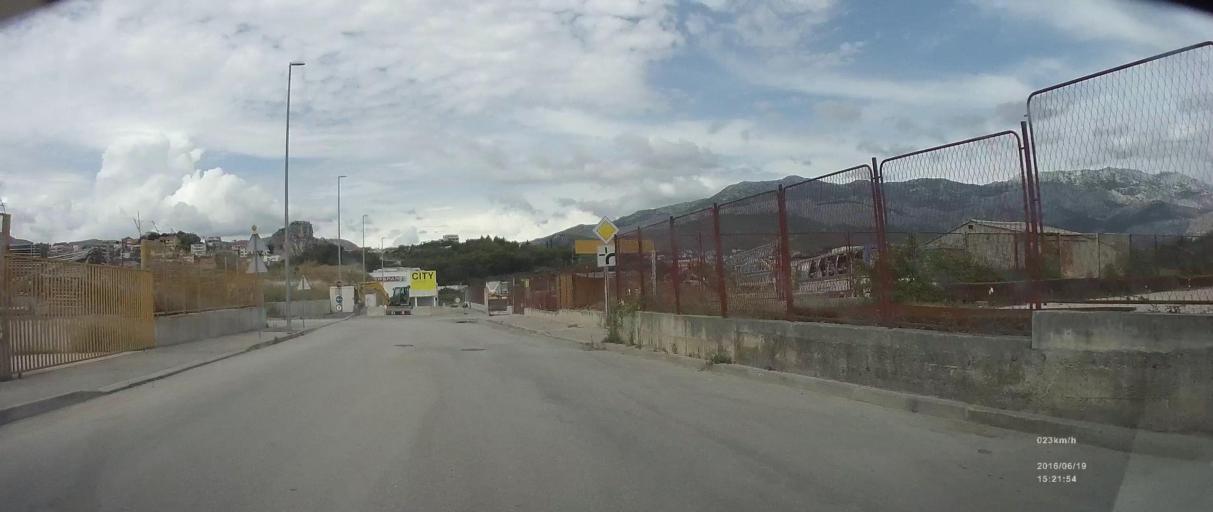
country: HR
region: Splitsko-Dalmatinska
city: Kamen
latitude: 43.5100
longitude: 16.5027
